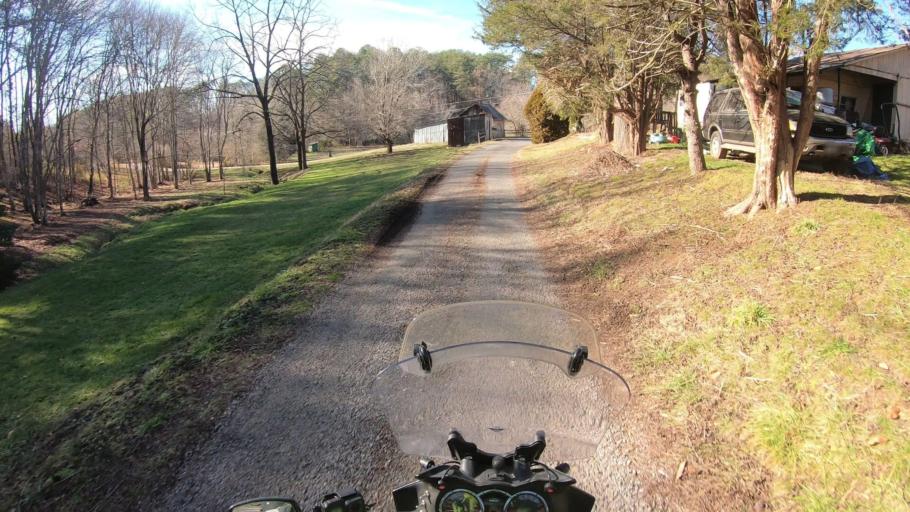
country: US
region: Georgia
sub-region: Fannin County
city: McCaysville
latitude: 34.9983
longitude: -84.3283
